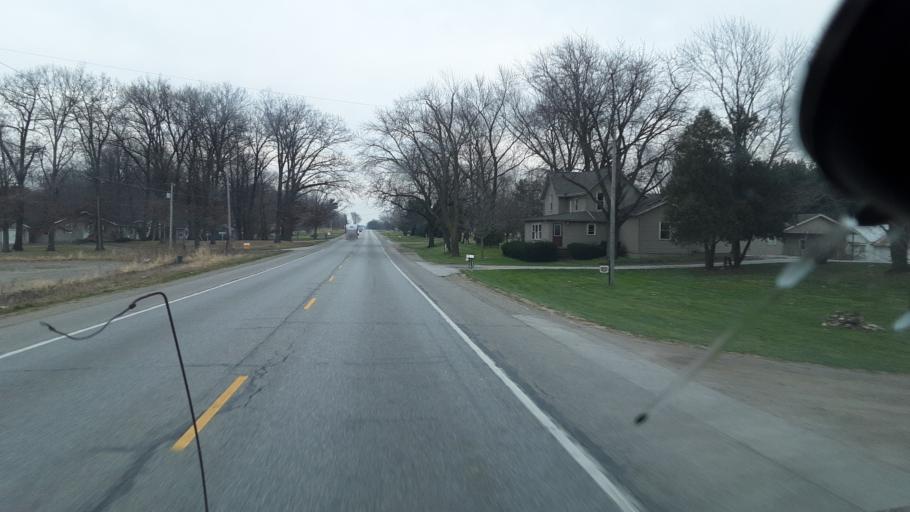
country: US
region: Indiana
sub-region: Elkhart County
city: Middlebury
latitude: 41.6678
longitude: -85.7558
